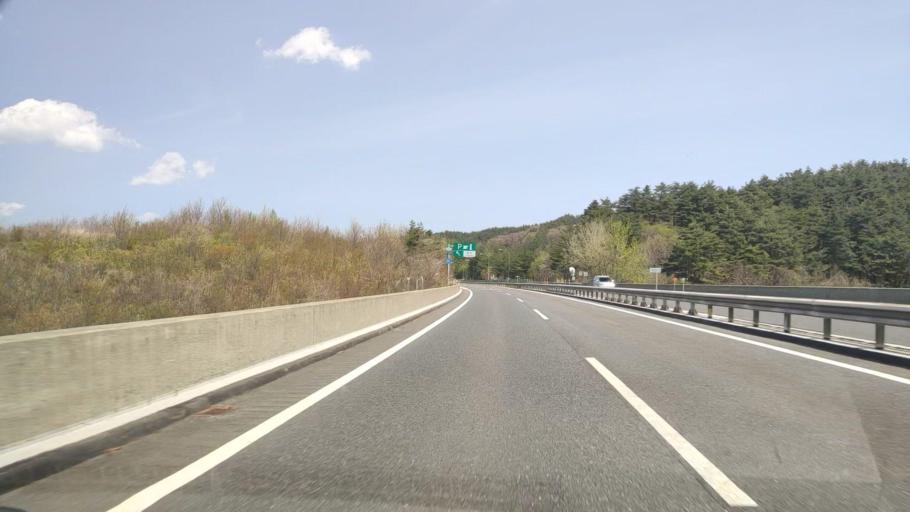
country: JP
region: Iwate
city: Ichinohe
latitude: 40.2929
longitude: 141.4210
